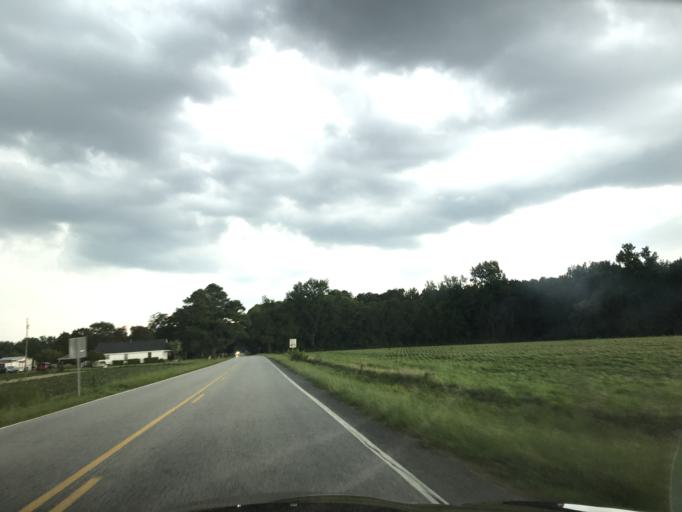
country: US
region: North Carolina
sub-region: Johnston County
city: Wilsons Mills
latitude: 35.5423
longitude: -78.4199
